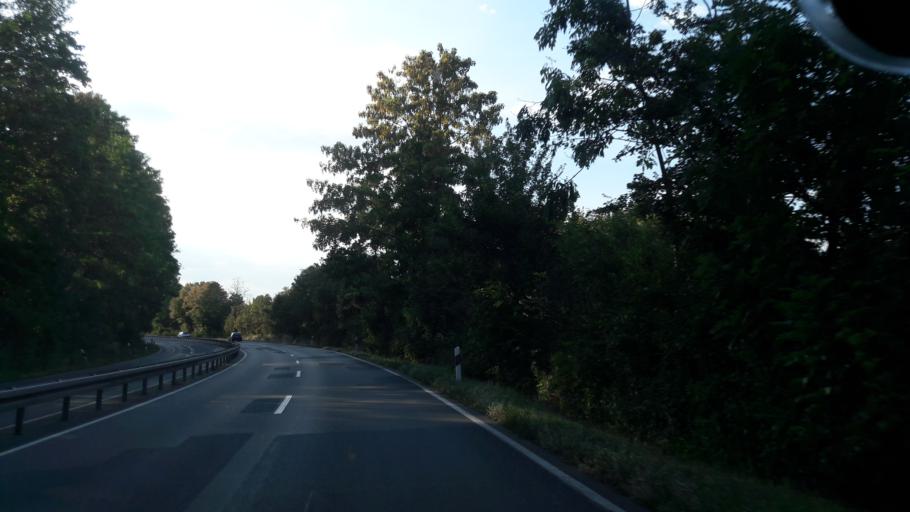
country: DE
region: Lower Saxony
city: Hildesheim
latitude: 52.1708
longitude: 9.9555
